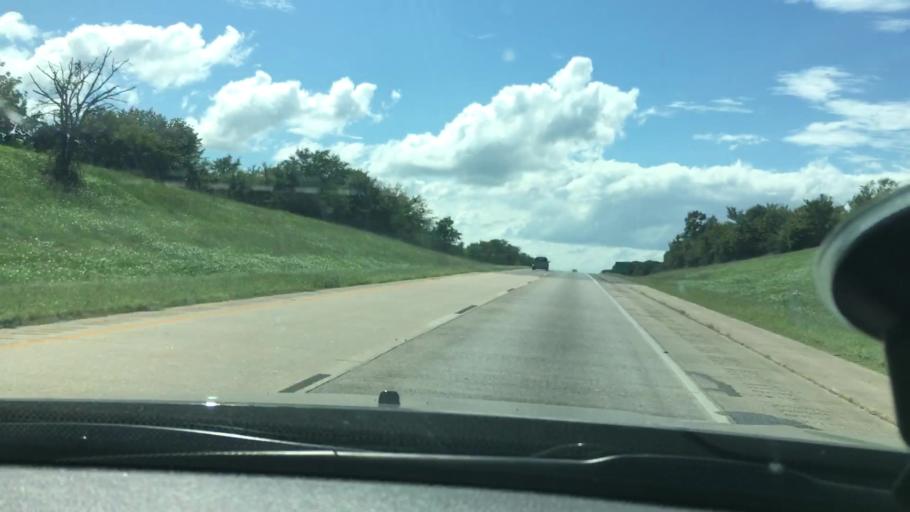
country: US
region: Oklahoma
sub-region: Sequoyah County
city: Vian
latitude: 35.4914
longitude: -95.0608
